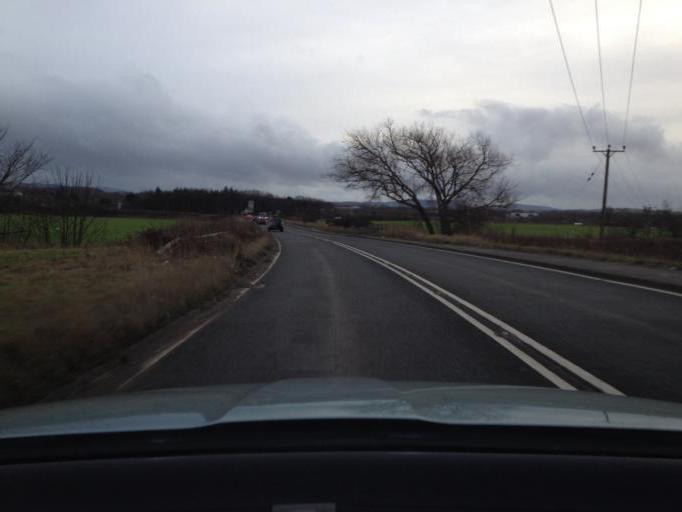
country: GB
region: Scotland
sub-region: Edinburgh
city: Kirkliston
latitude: 55.9444
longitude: -3.4142
